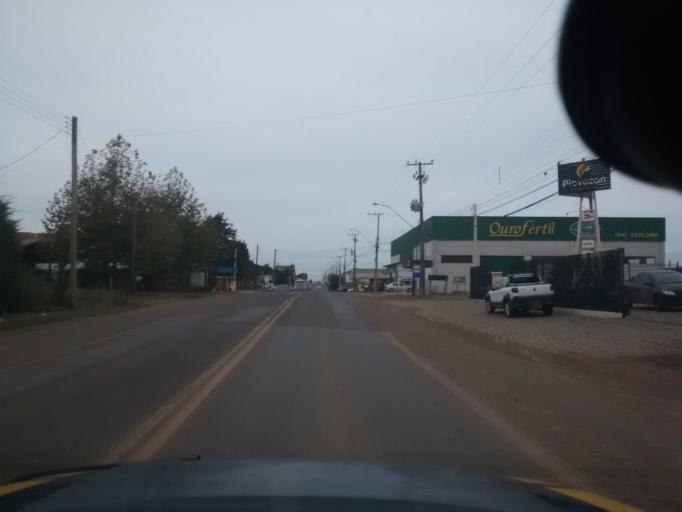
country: BR
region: Rio Grande do Sul
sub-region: Vacaria
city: Vacaria
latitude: -28.4951
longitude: -50.9537
